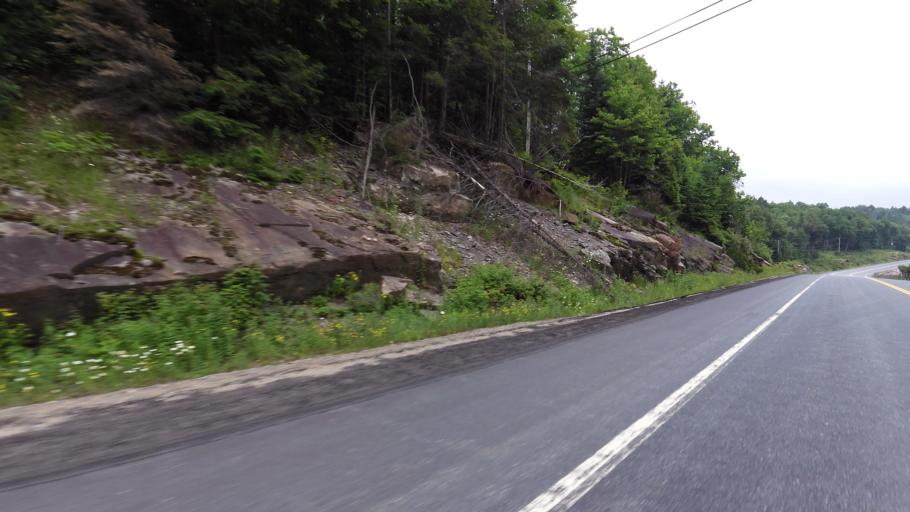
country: CA
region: Ontario
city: Huntsville
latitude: 45.5357
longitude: -78.7026
